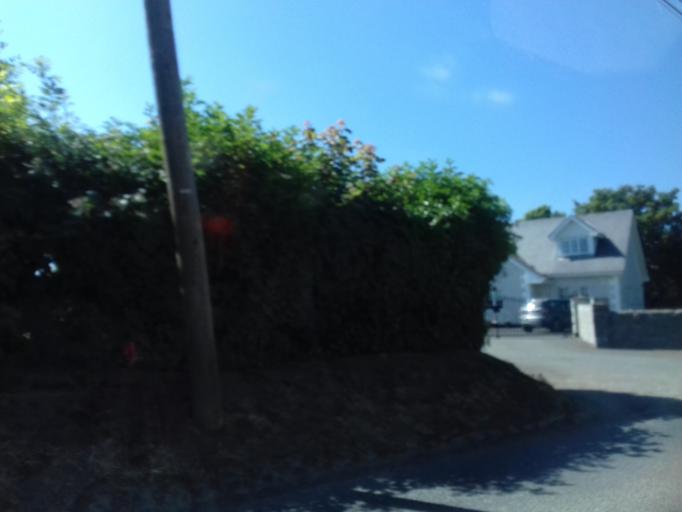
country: IE
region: Leinster
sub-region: An Mhi
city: Stamullin
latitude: 53.5751
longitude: -6.2838
